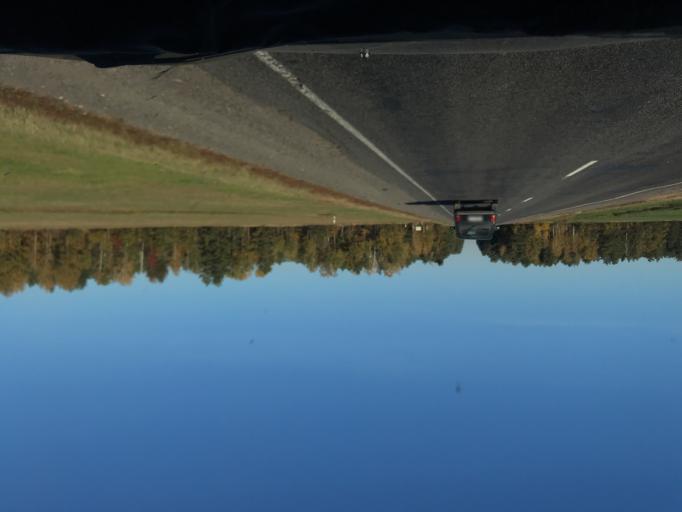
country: BY
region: Gomel
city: Kalinkavichy
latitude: 52.0519
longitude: 29.3611
